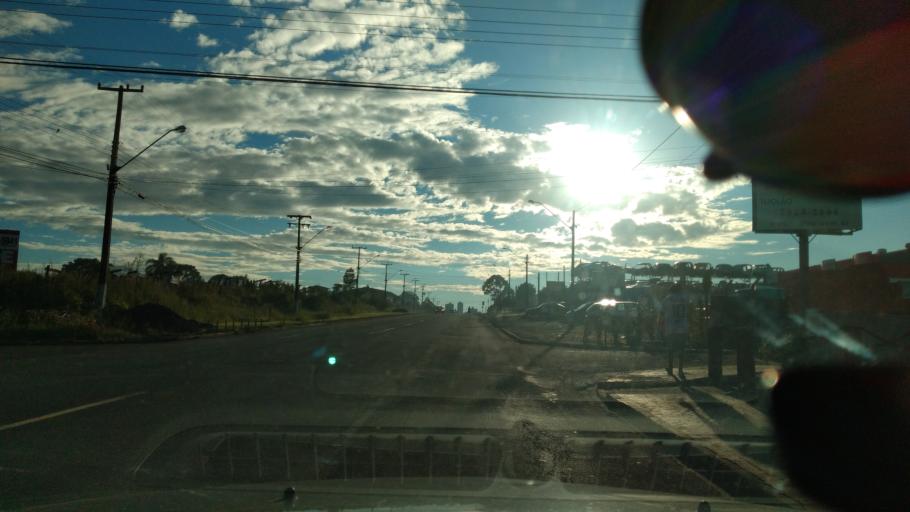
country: BR
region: Parana
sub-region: Guarapuava
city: Guarapuava
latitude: -25.3936
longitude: -51.4912
